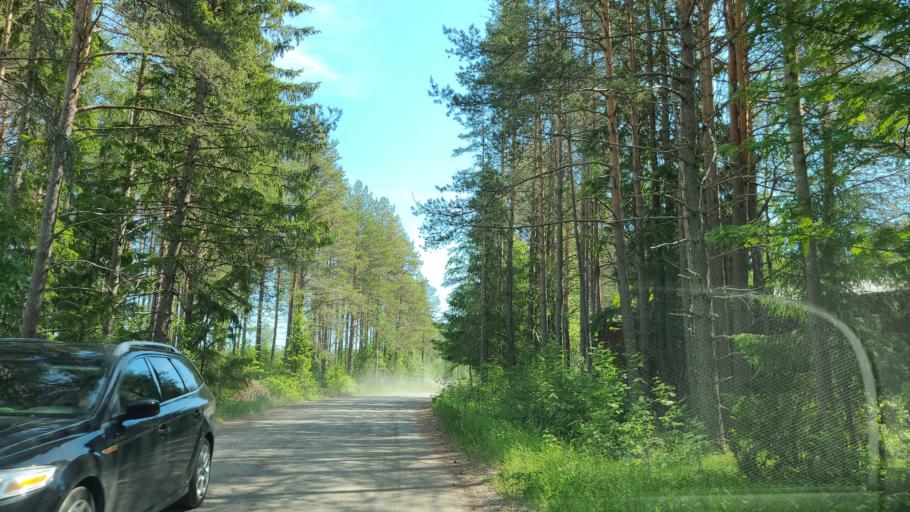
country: SE
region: Vaesterbotten
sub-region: Robertsfors Kommun
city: Robertsfors
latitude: 64.2259
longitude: 21.0217
